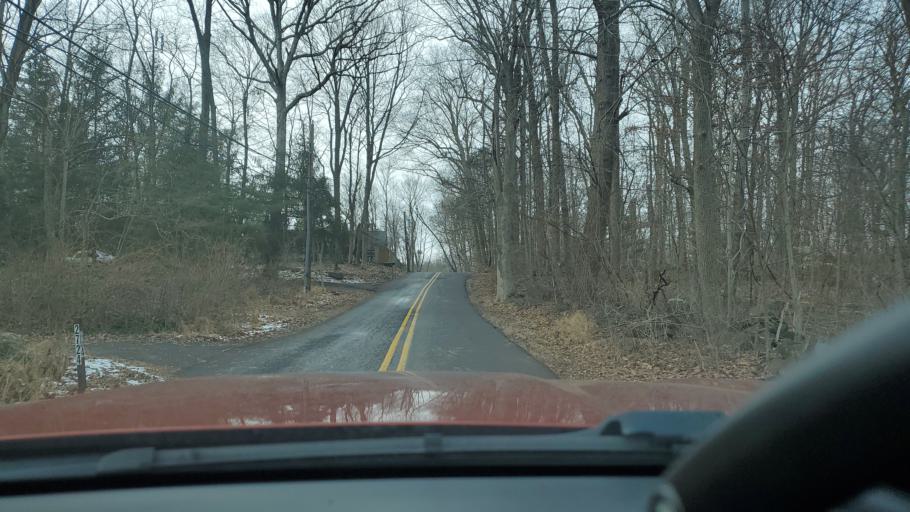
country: US
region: Pennsylvania
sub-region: Montgomery County
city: Red Hill
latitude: 40.3265
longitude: -75.5085
